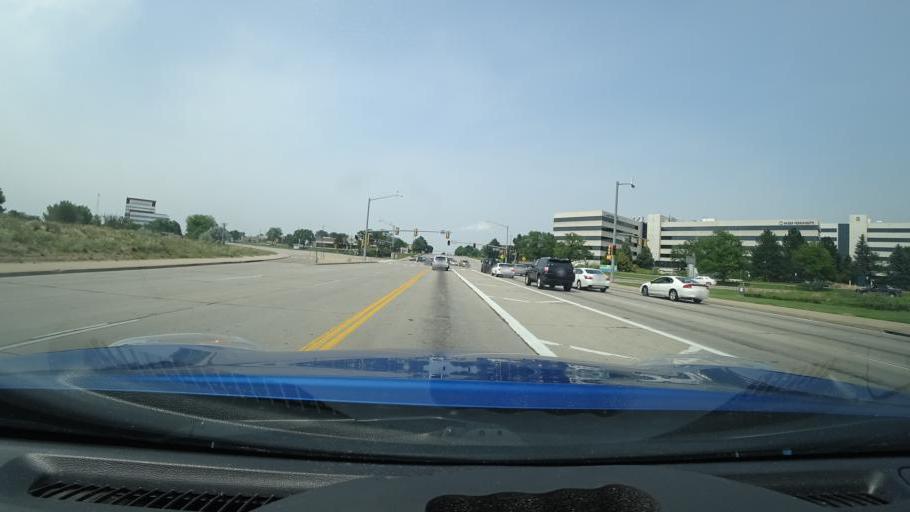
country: US
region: Colorado
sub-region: Adams County
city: Aurora
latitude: 39.6701
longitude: -104.8661
